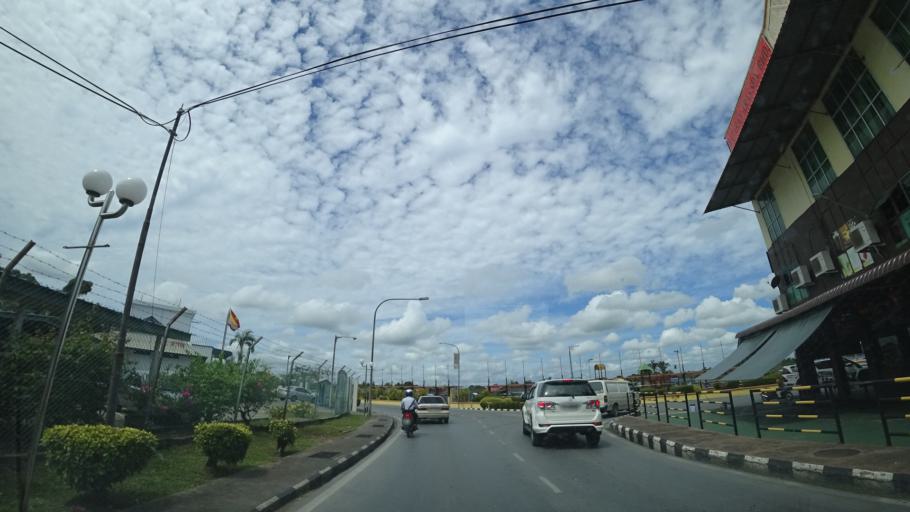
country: MY
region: Sarawak
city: Limbang
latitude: 4.7516
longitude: 115.0087
